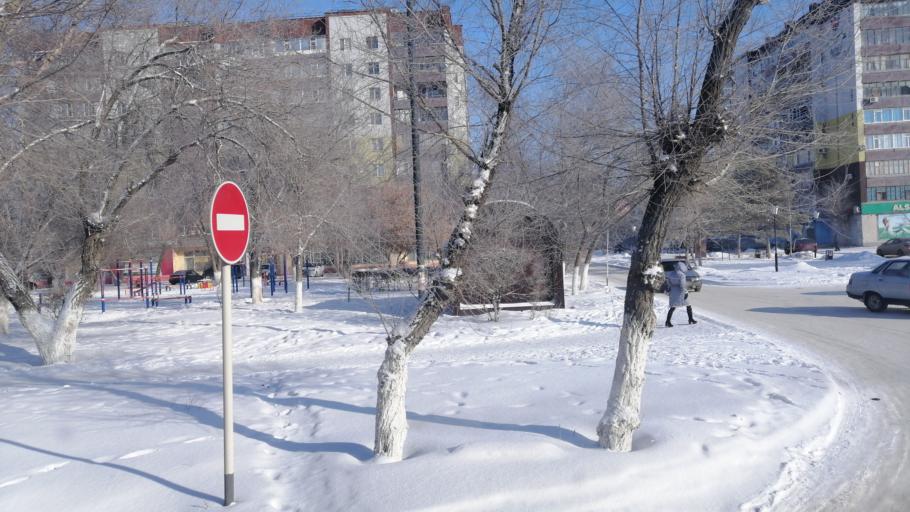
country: KZ
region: Aqtoebe
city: Aqtobe
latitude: 50.2821
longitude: 57.2160
